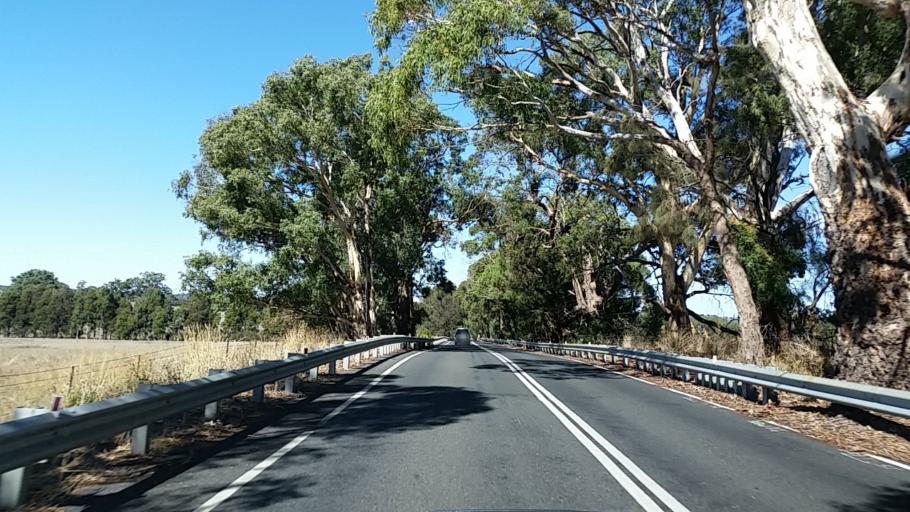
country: AU
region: South Australia
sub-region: Adelaide Hills
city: Birdwood
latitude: -34.7628
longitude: 139.0143
